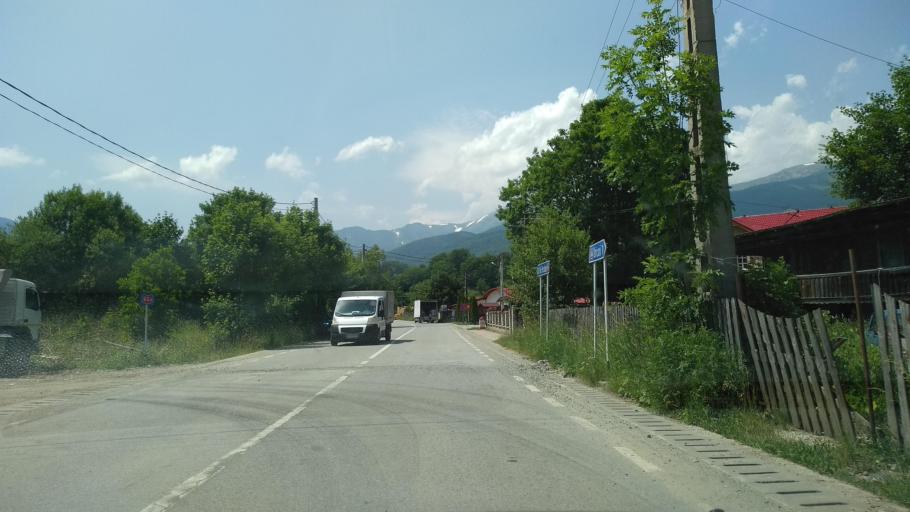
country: RO
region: Hunedoara
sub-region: Comuna Uricani
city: Uricani
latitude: 45.3042
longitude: 23.0356
